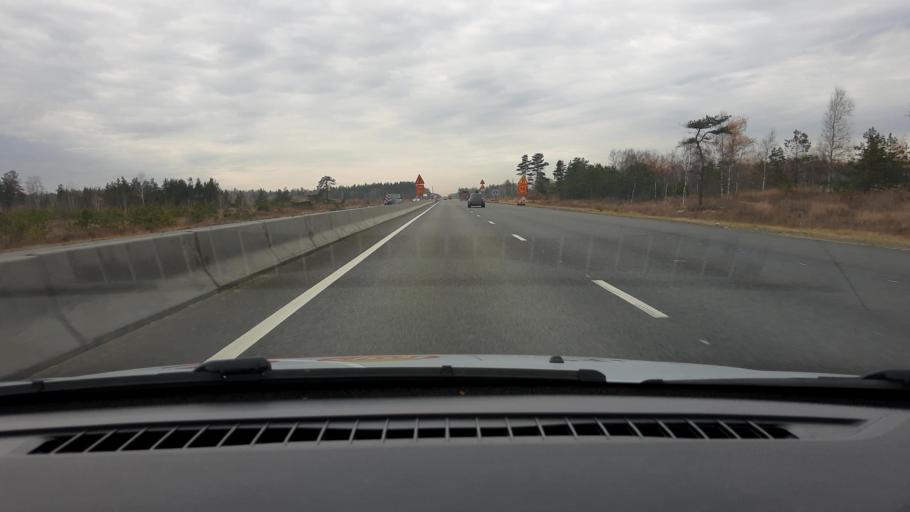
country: RU
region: Nizjnij Novgorod
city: Dzerzhinsk
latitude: 56.3004
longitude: 43.5234
